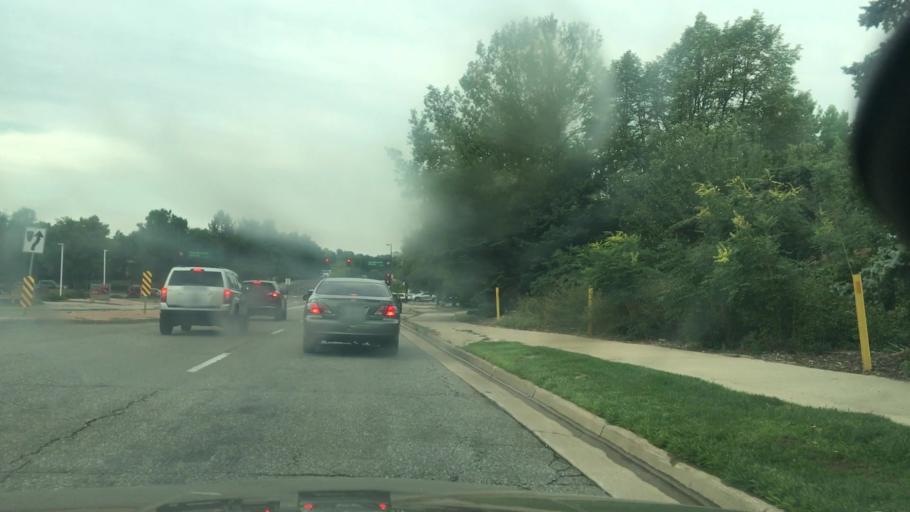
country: US
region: Colorado
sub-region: Arapahoe County
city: Castlewood
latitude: 39.6253
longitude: -104.8854
